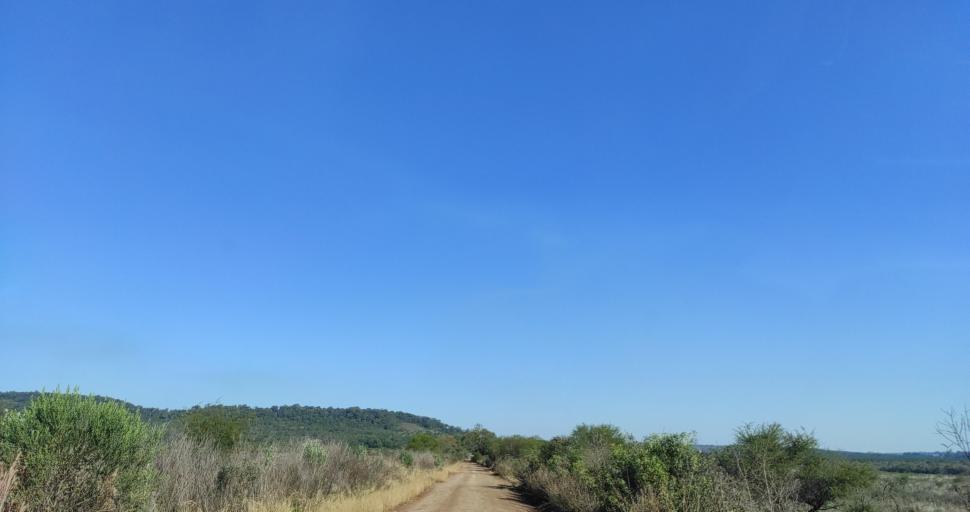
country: AR
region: Misiones
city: Cerro Cora
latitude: -27.6579
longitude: -55.6588
